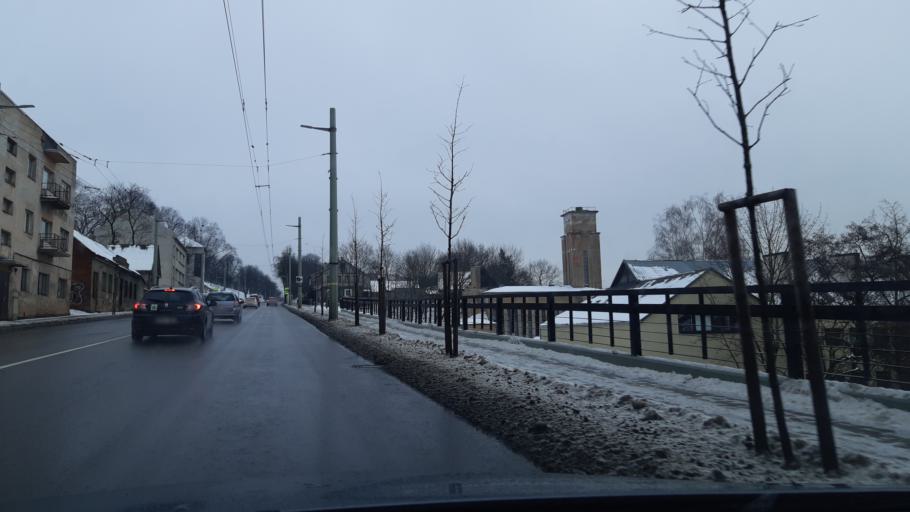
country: LT
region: Kauno apskritis
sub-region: Kaunas
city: Kaunas
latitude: 54.9001
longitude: 23.9058
